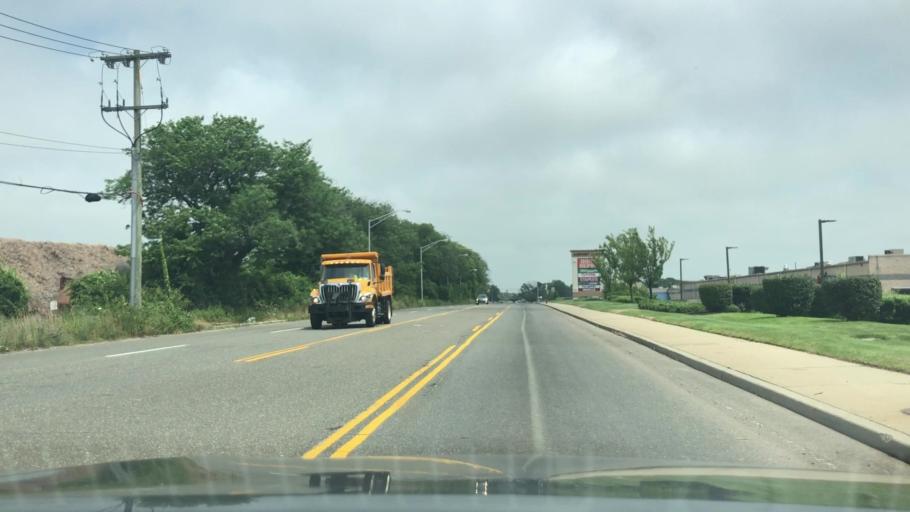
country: US
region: New York
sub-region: Suffolk County
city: East Farmingdale
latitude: 40.7396
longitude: -73.4196
